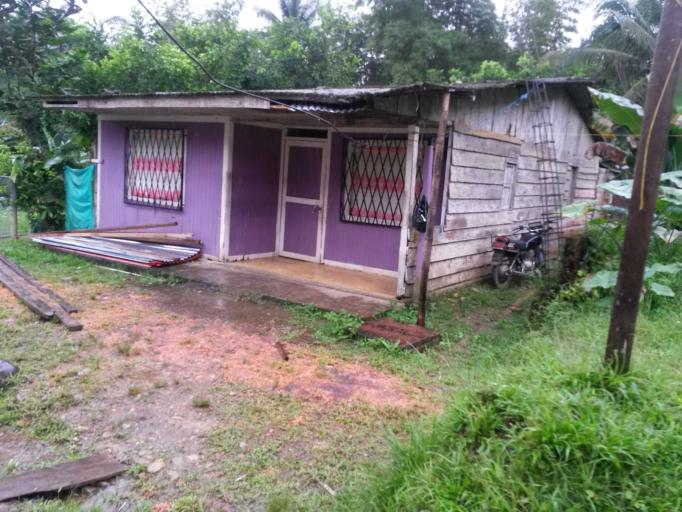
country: CO
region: Valle del Cauca
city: Buenaventura
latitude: 3.8416
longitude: -76.8995
